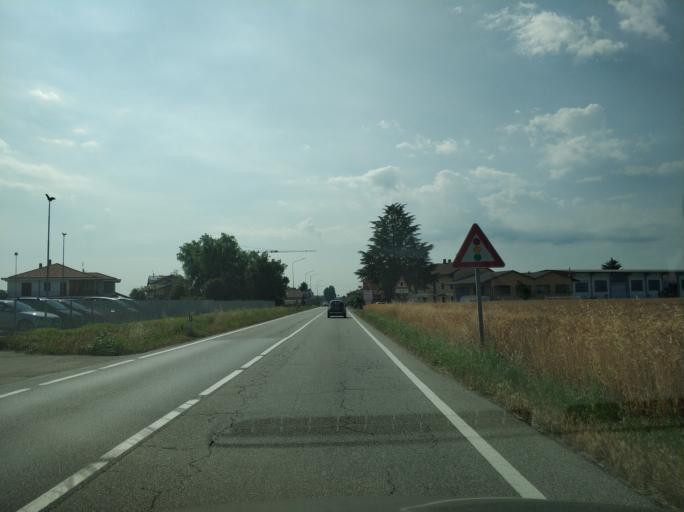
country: IT
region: Piedmont
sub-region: Provincia di Torino
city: Marocchi
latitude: 44.9447
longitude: 7.8115
